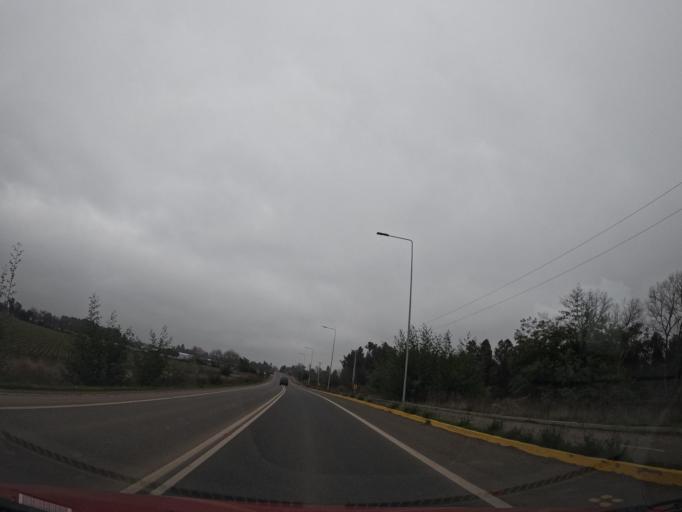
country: CL
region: Maule
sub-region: Provincia de Talca
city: San Clemente
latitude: -35.5458
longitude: -71.4730
